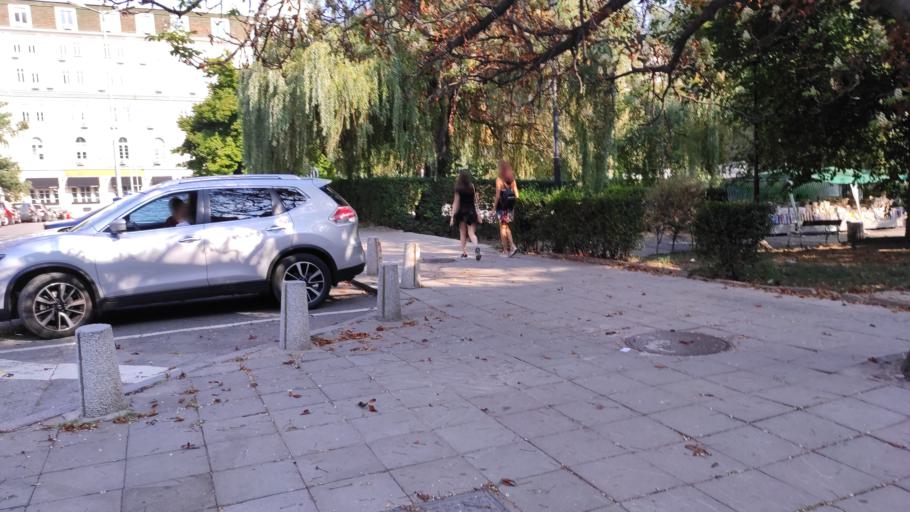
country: BG
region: Sofia-Capital
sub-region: Stolichna Obshtina
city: Sofia
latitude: 42.6954
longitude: 23.3225
